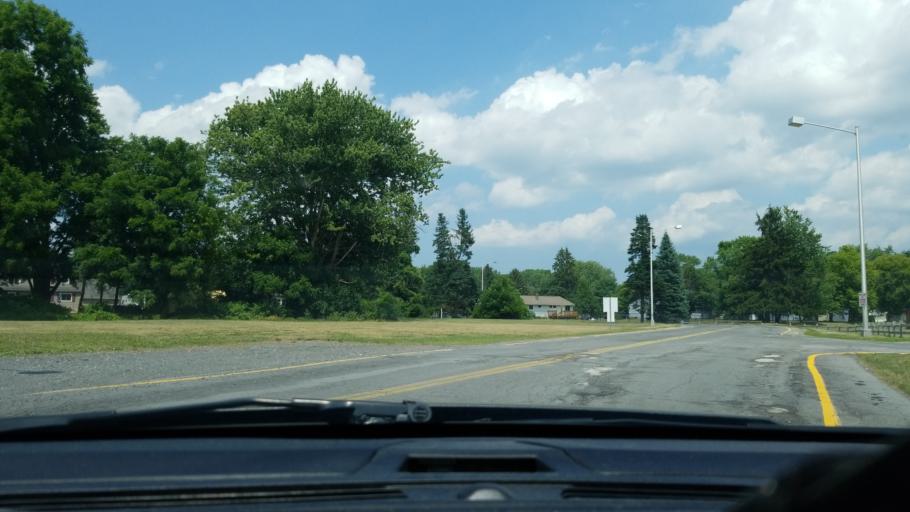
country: US
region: New York
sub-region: Onondaga County
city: Liverpool
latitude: 43.1490
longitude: -76.2115
